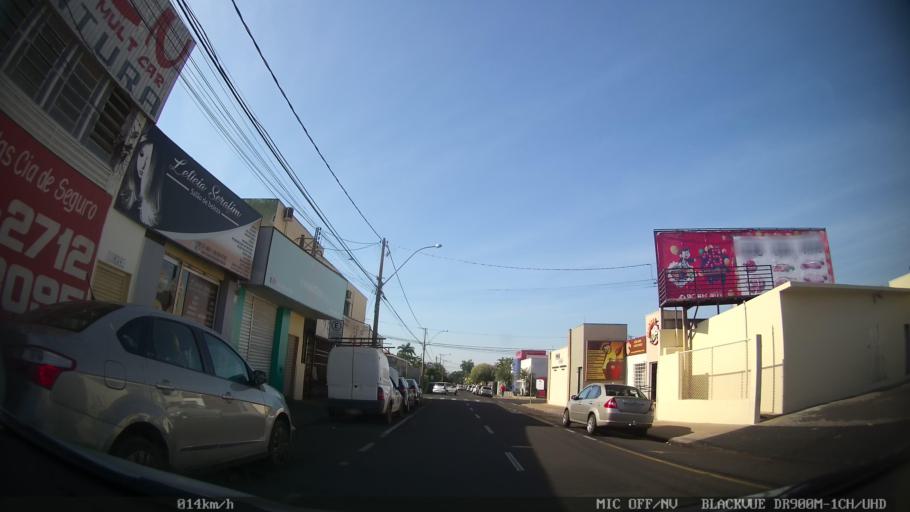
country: BR
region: Sao Paulo
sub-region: Sao Jose Do Rio Preto
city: Sao Jose do Rio Preto
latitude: -20.8051
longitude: -49.3875
